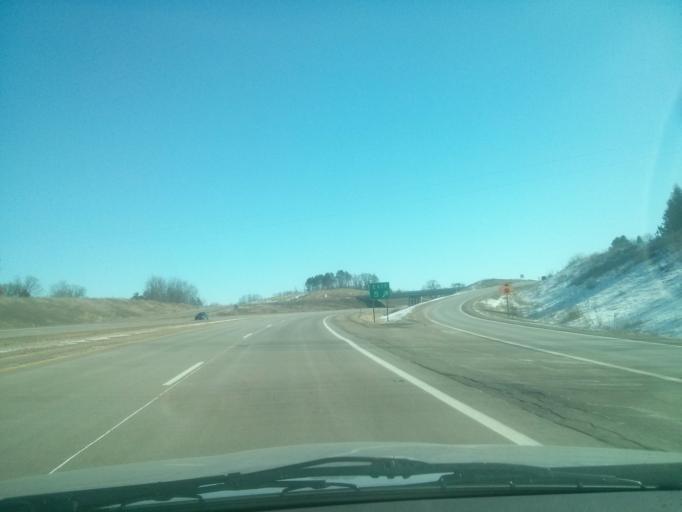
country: US
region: Wisconsin
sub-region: Saint Croix County
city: Somerset
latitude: 45.1056
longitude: -92.7277
